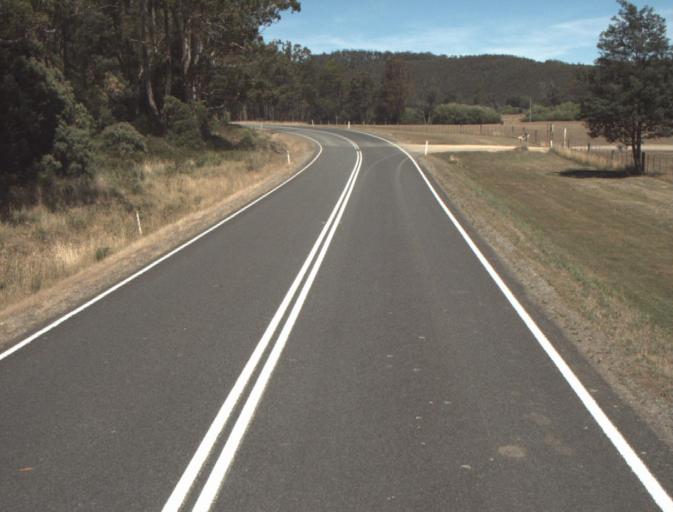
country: AU
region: Tasmania
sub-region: Dorset
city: Scottsdale
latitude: -41.3010
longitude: 147.3822
